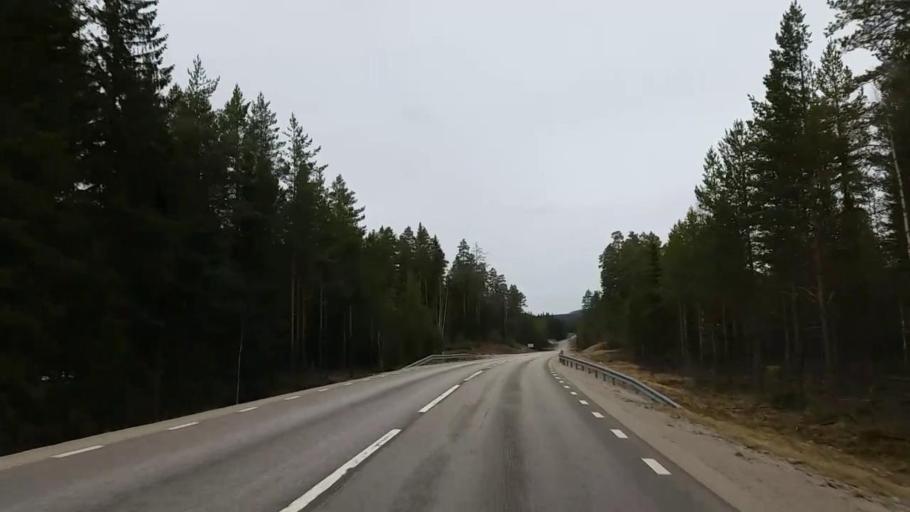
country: SE
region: Gaevleborg
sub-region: Bollnas Kommun
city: Vittsjo
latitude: 61.1606
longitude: 15.8818
